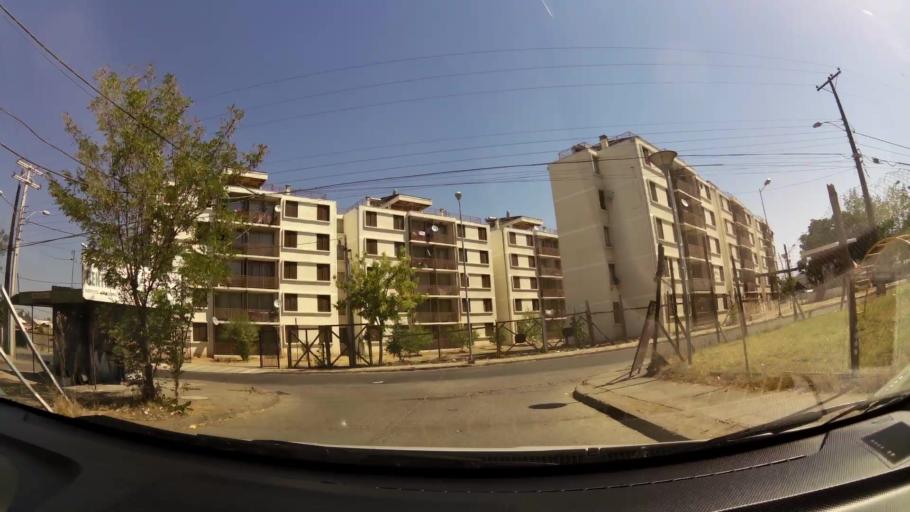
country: CL
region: Maule
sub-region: Provincia de Talca
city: Talca
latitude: -35.4134
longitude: -71.6521
